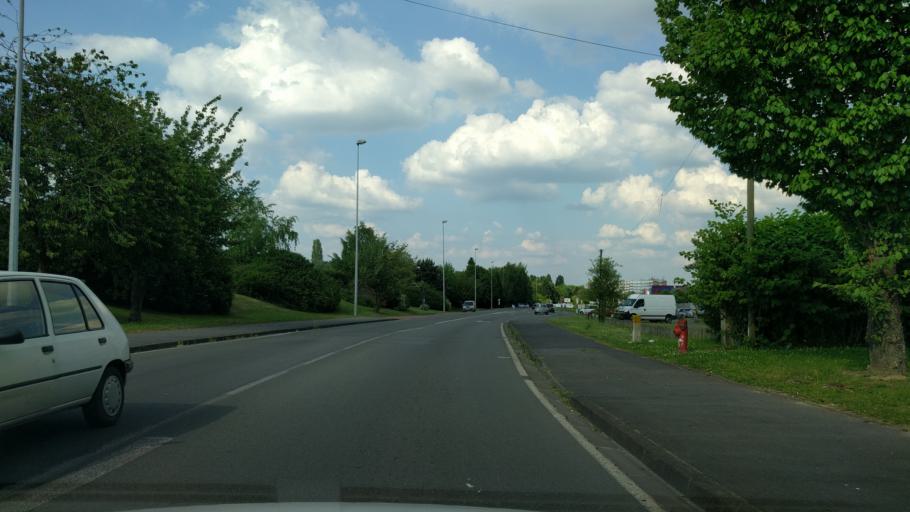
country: FR
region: Nord-Pas-de-Calais
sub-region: Departement du Nord
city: Raismes
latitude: 50.3845
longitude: 3.4844
